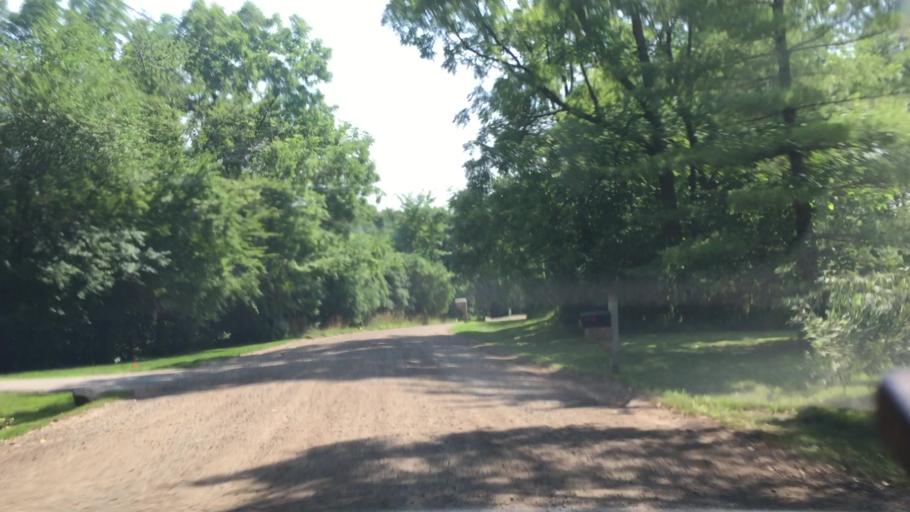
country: US
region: Michigan
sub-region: Oakland County
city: Orchard Lake
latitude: 42.5546
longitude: -83.3353
